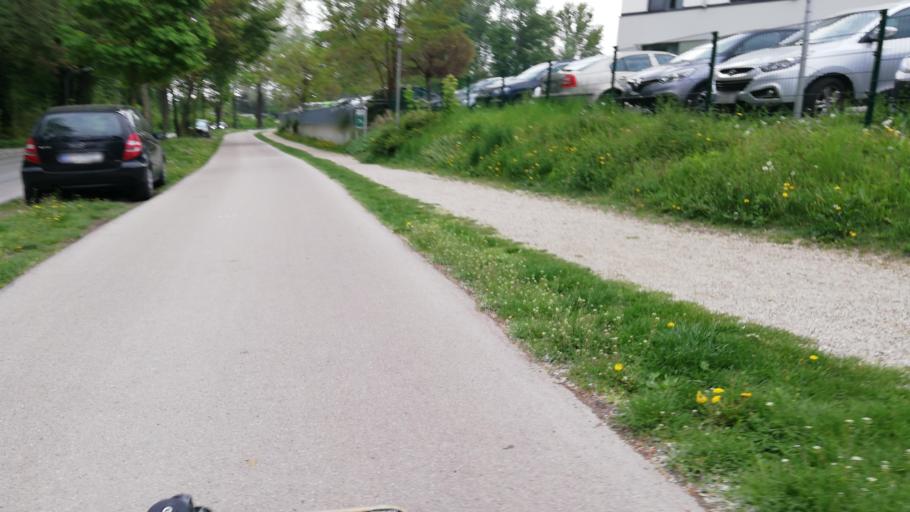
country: AT
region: Lower Austria
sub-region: Politischer Bezirk Wien-Umgebung
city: Klosterneuburg
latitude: 48.3104
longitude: 16.3312
